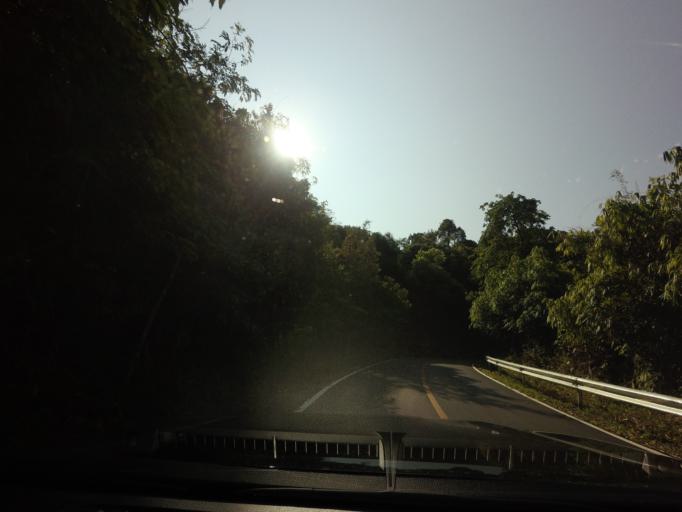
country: TH
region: Kanchanaburi
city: Thong Pha Phum
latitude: 14.6861
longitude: 98.4159
